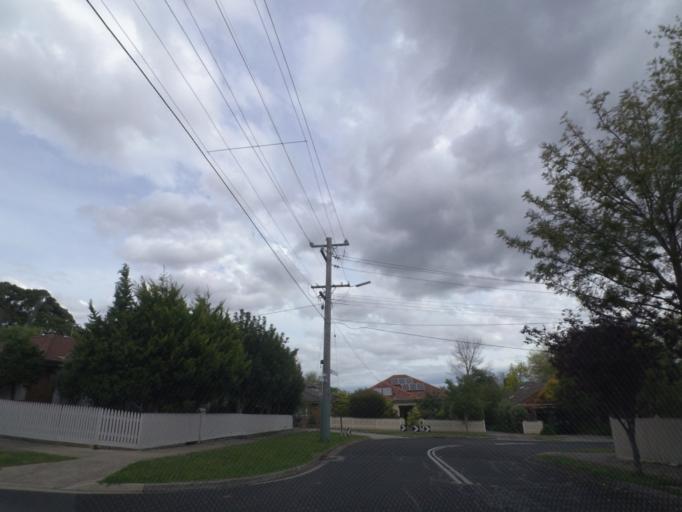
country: AU
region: Victoria
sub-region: Whitehorse
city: Box Hill
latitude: -37.8261
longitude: 145.1283
